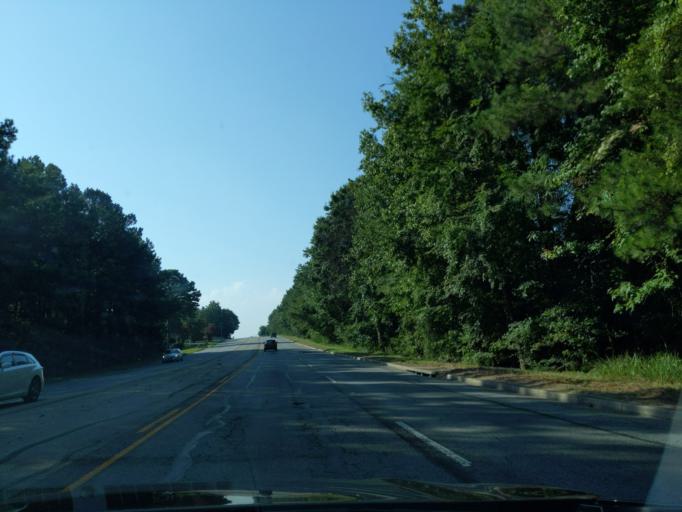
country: US
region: South Carolina
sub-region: Newberry County
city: Prosperity
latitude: 34.2435
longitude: -81.5678
